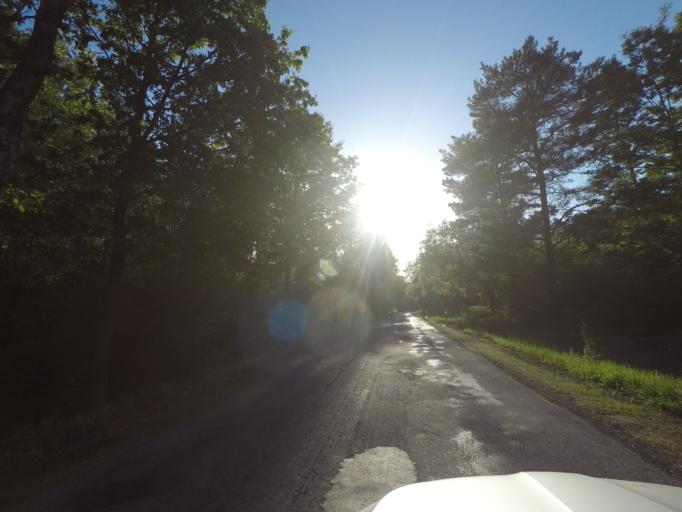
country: DE
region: Brandenburg
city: Bad Freienwalde
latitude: 52.8161
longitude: 14.0257
